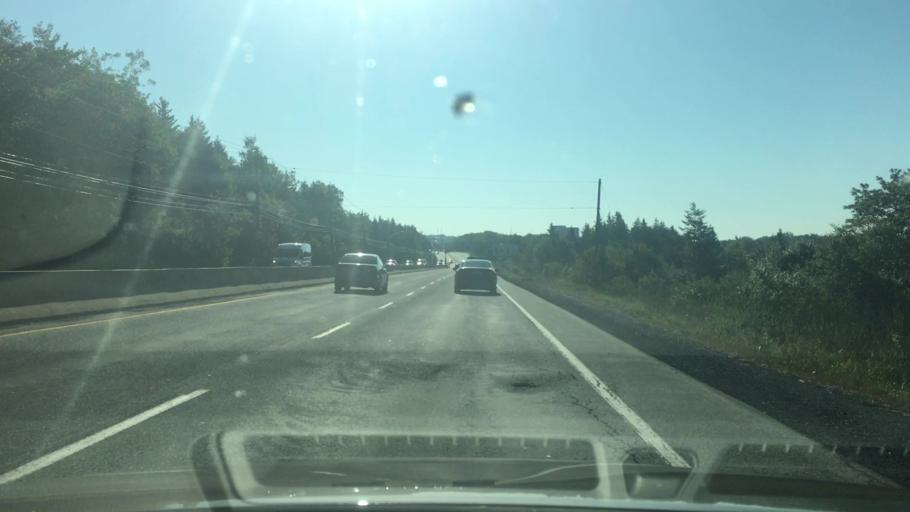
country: CA
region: Nova Scotia
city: Dartmouth
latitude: 44.7076
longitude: -63.6219
